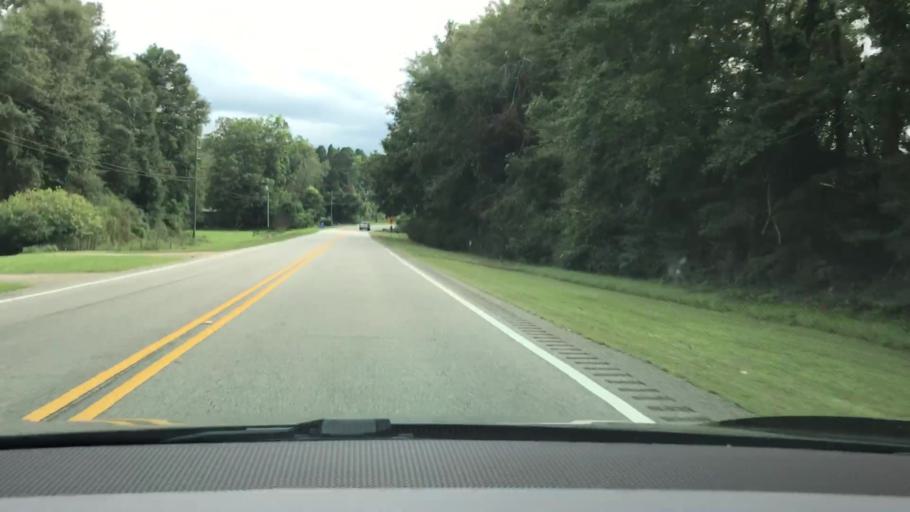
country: US
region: Alabama
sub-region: Coffee County
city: Elba
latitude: 31.5380
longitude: -86.0264
